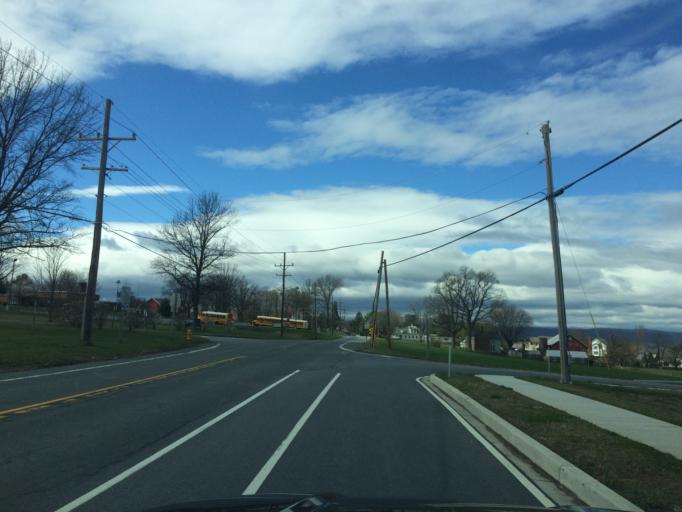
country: US
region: Maryland
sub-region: Frederick County
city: Jefferson
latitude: 39.3604
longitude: -77.5462
